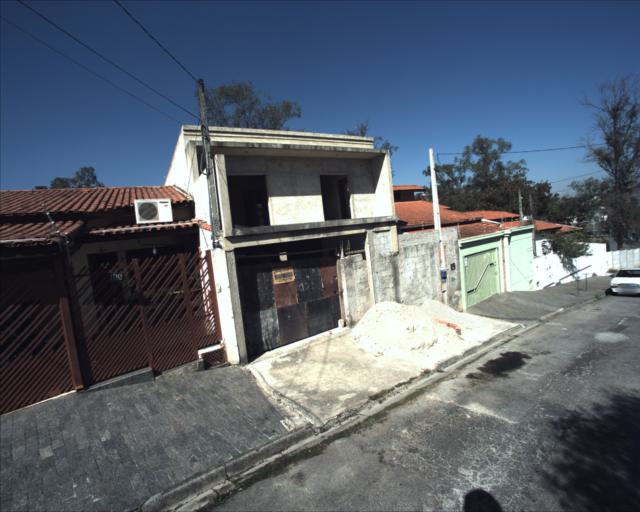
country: BR
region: Sao Paulo
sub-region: Sorocaba
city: Sorocaba
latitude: -23.5115
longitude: -47.4270
